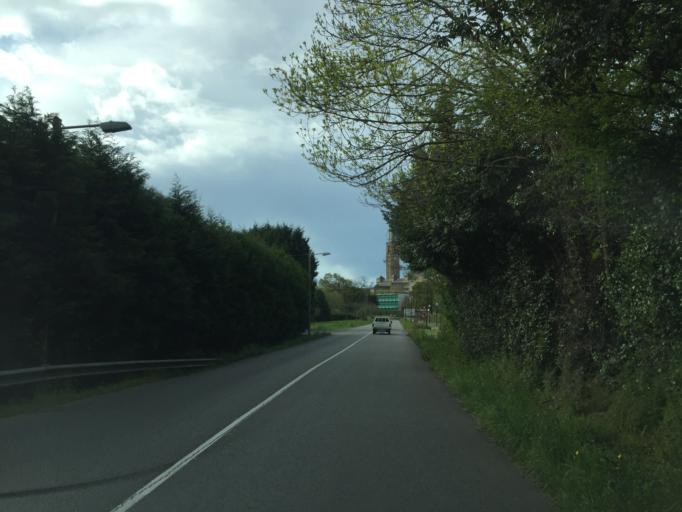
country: ES
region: Asturias
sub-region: Province of Asturias
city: Gijon
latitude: 43.5201
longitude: -5.6096
